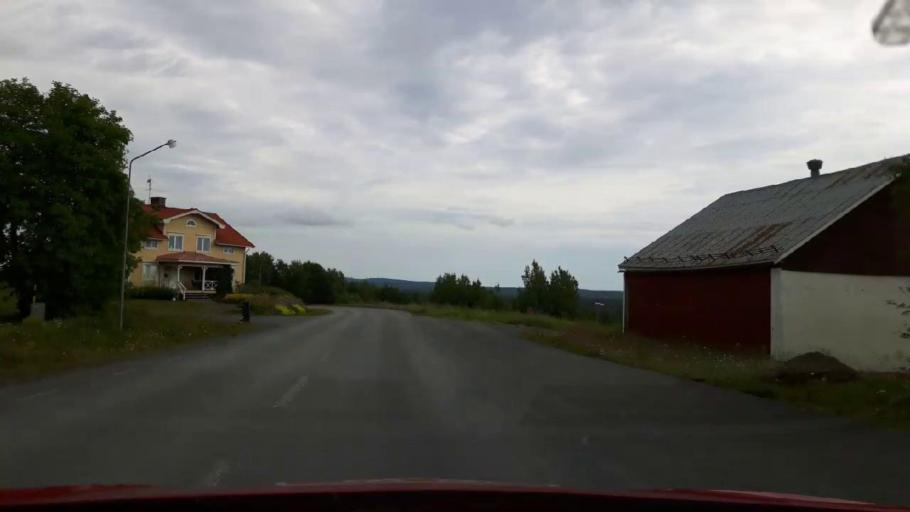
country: SE
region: Jaemtland
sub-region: OEstersunds Kommun
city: Lit
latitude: 63.4218
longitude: 15.2579
